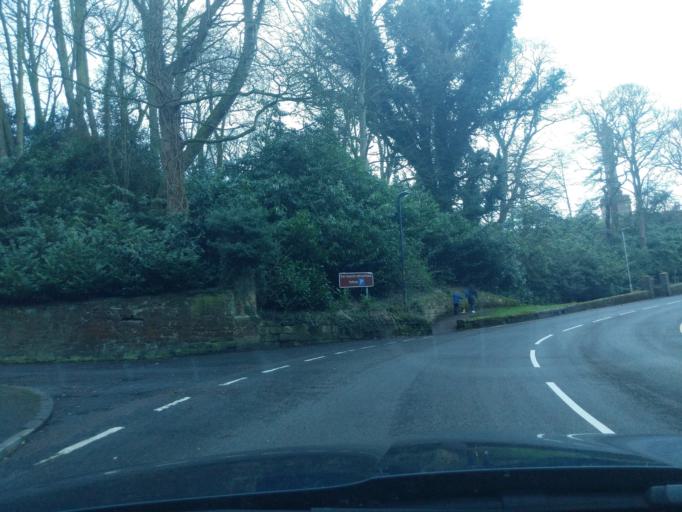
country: GB
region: England
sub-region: Northumberland
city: Alnwick
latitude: 55.4118
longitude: -1.6978
